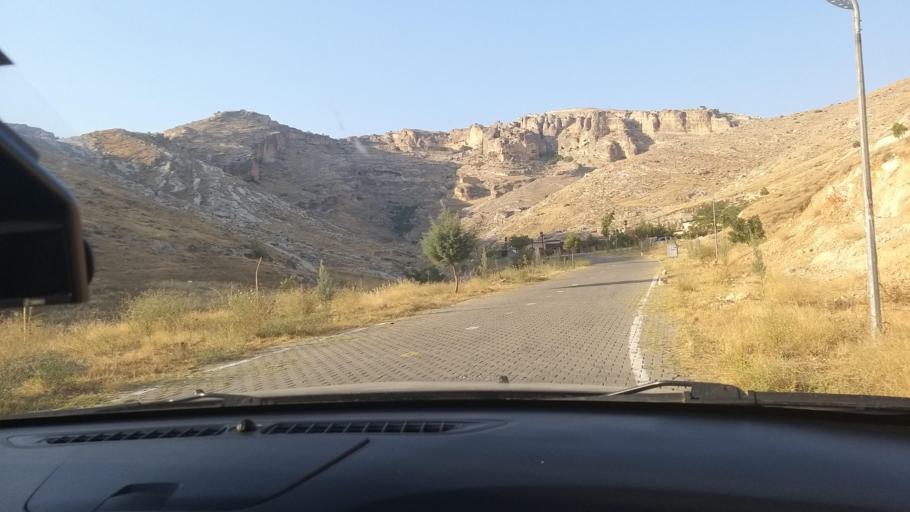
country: TR
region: Diyarbakir
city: Silvan
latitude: 38.1299
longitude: 41.0880
